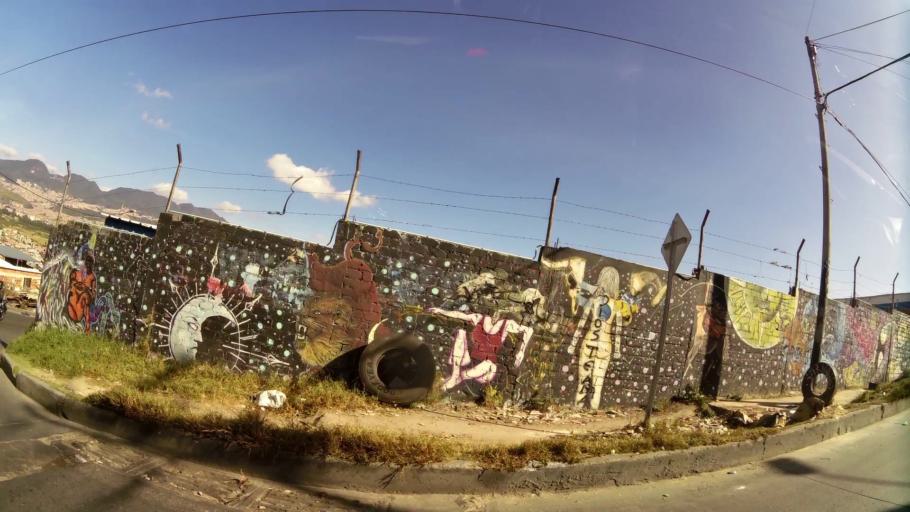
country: CO
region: Cundinamarca
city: Soacha
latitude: 4.5535
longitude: -74.1436
